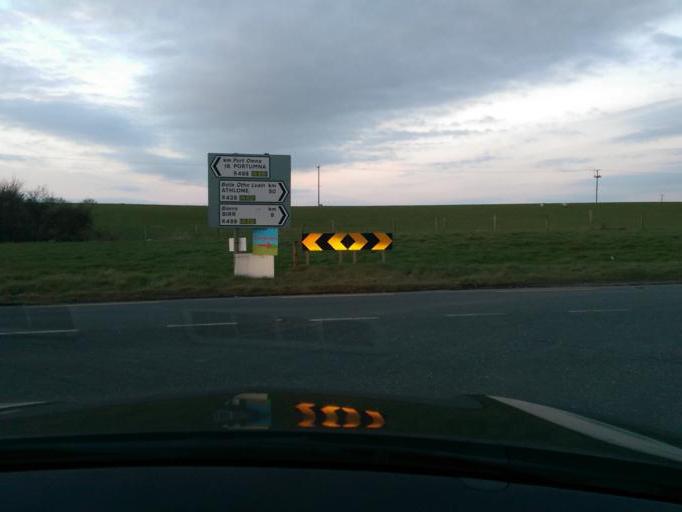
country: IE
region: Leinster
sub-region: Uibh Fhaili
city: Banagher
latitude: 53.1018
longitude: -8.0068
